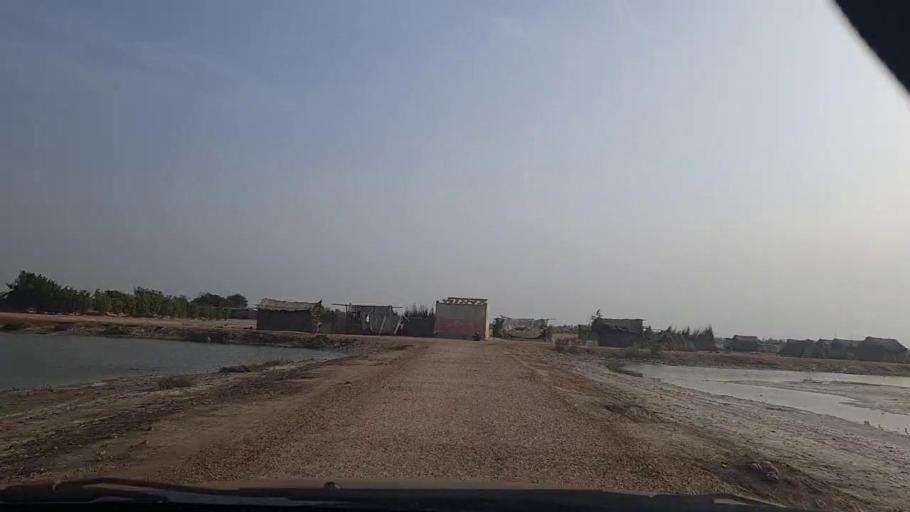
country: PK
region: Sindh
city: Thatta
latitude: 24.7235
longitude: 67.9027
